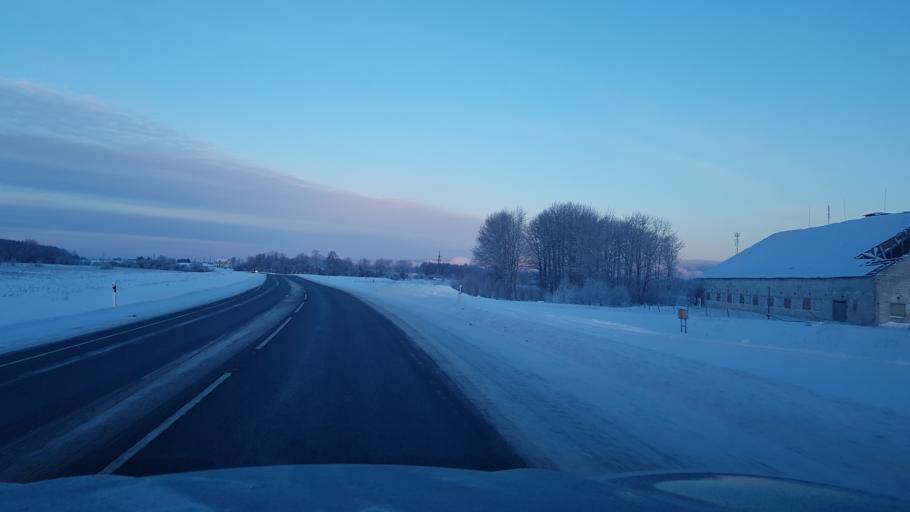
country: EE
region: Ida-Virumaa
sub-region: Narva-Joesuu linn
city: Narva-Joesuu
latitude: 59.3989
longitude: 28.0737
